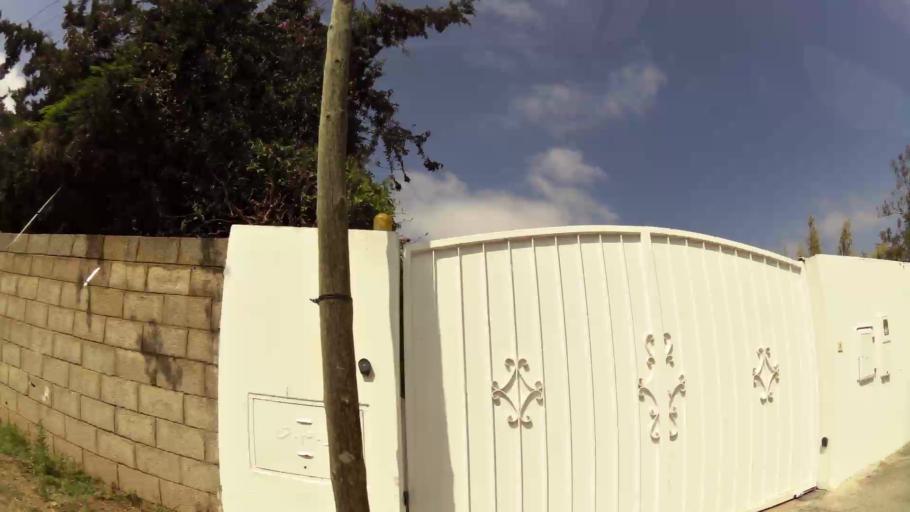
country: MA
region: Rabat-Sale-Zemmour-Zaer
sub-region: Rabat
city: Rabat
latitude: 33.9794
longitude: -6.8398
